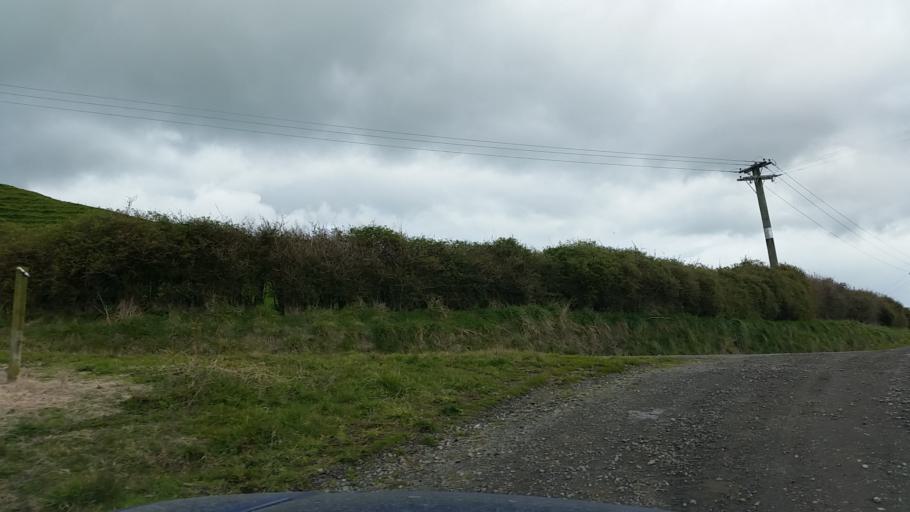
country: NZ
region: Taranaki
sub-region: South Taranaki District
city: Eltham
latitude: -39.3584
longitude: 174.3807
